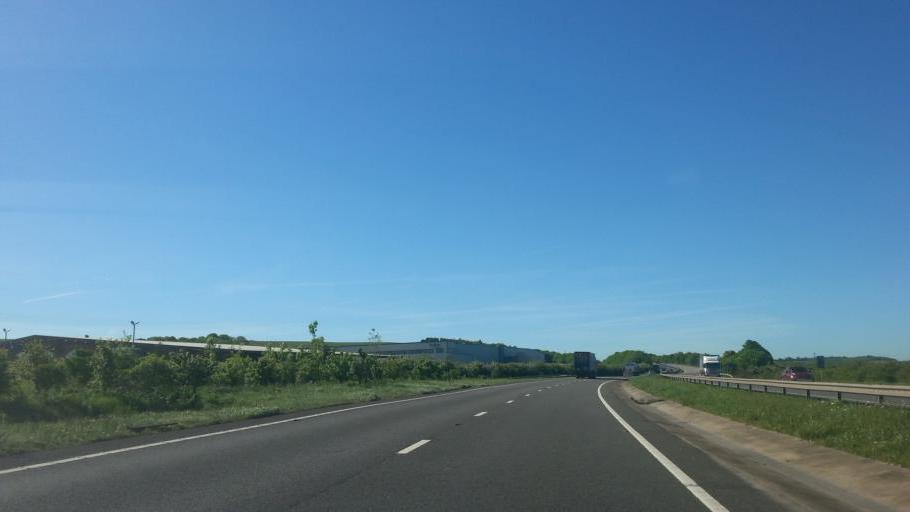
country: GB
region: England
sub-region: Lincolnshire
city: Great Gonerby
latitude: 52.9461
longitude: -0.6827
